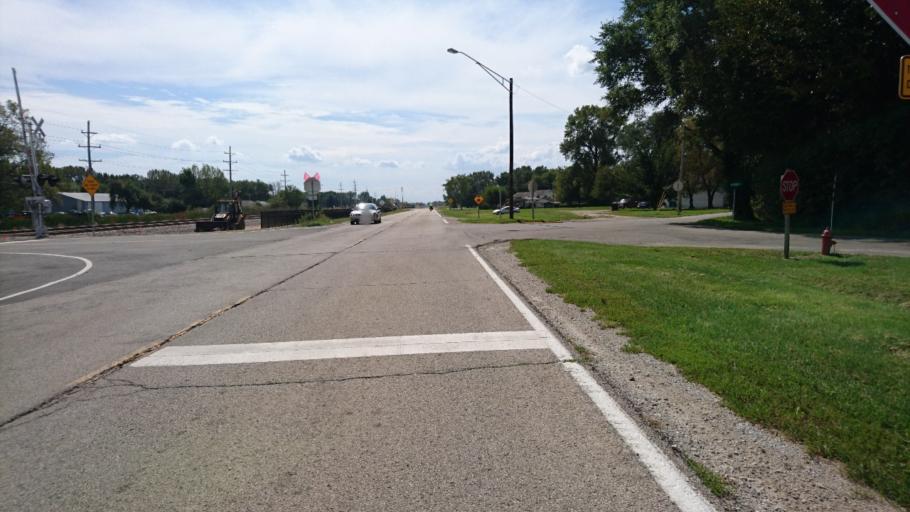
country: US
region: Illinois
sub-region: Grundy County
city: Central City
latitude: 41.2251
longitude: -88.2618
